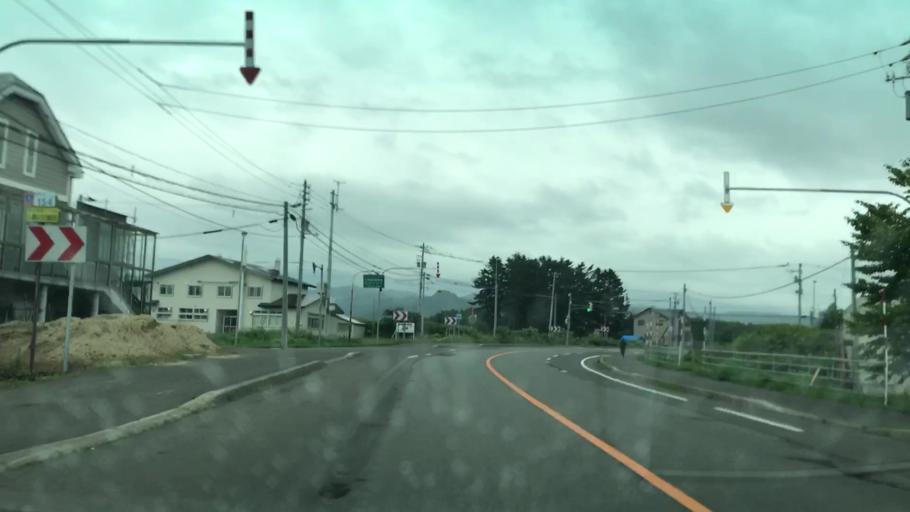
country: JP
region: Hokkaido
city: Niseko Town
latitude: 42.8128
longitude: 140.5439
